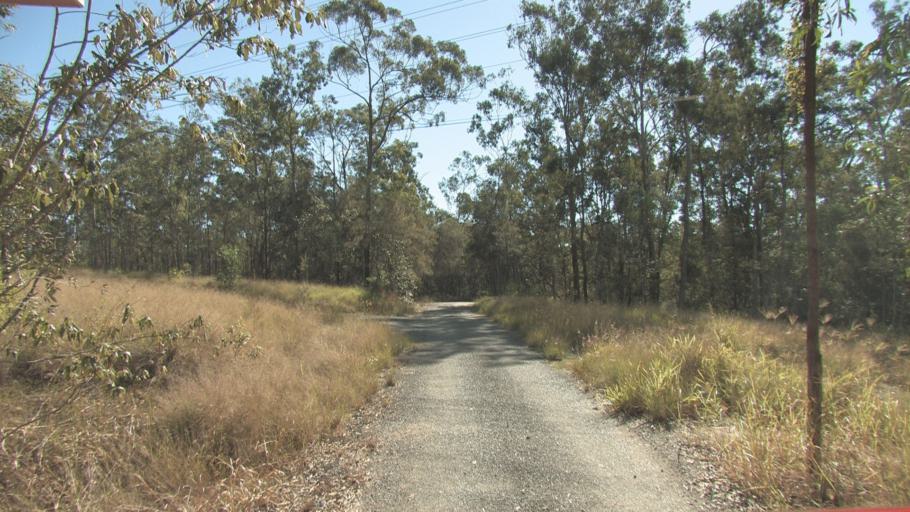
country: AU
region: Queensland
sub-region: Logan
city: Chambers Flat
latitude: -27.8036
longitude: 153.0878
